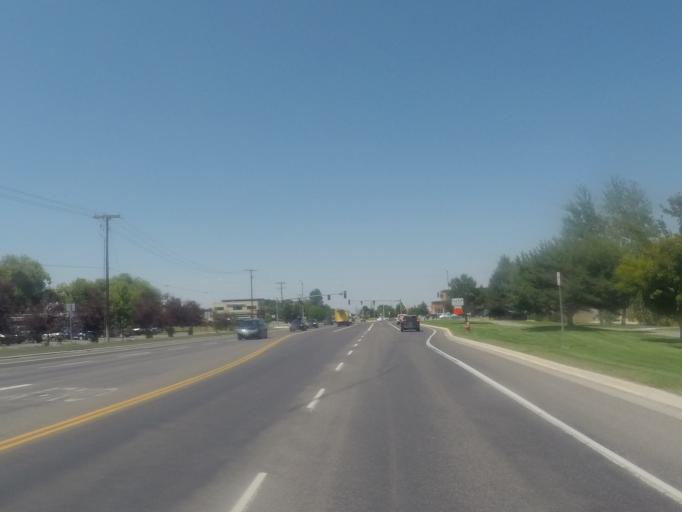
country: US
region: Montana
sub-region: Gallatin County
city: Bozeman
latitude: 45.6932
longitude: -111.0604
